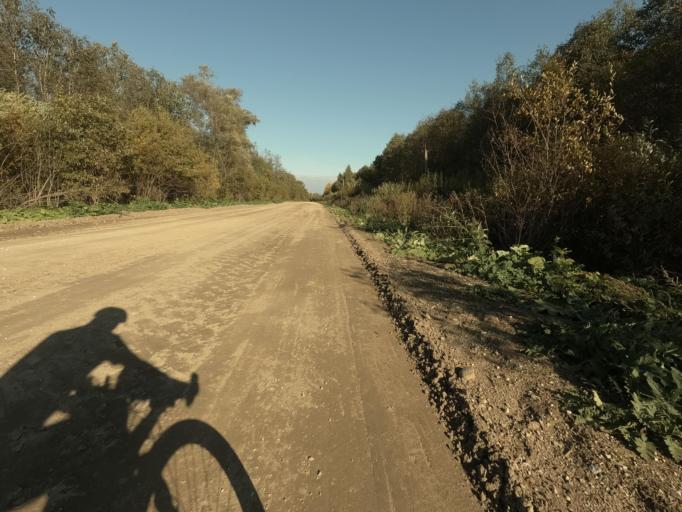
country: RU
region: Novgorod
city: Batetskiy
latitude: 58.8750
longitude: 30.7253
